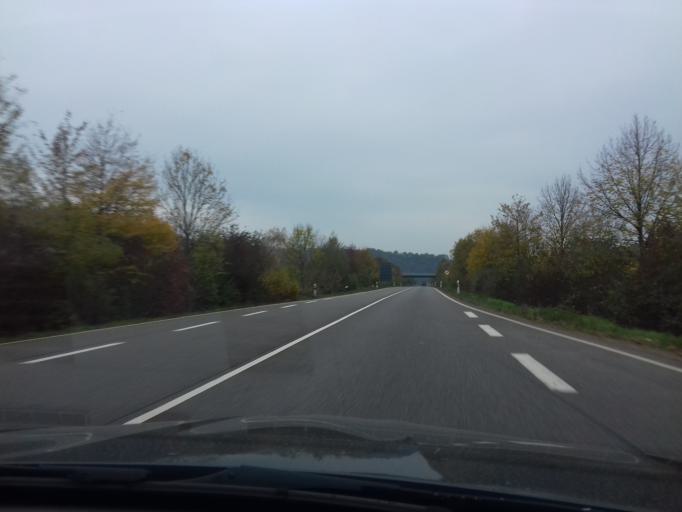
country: DE
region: Rheinland-Pfalz
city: Ockfen
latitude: 49.6100
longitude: 6.5672
